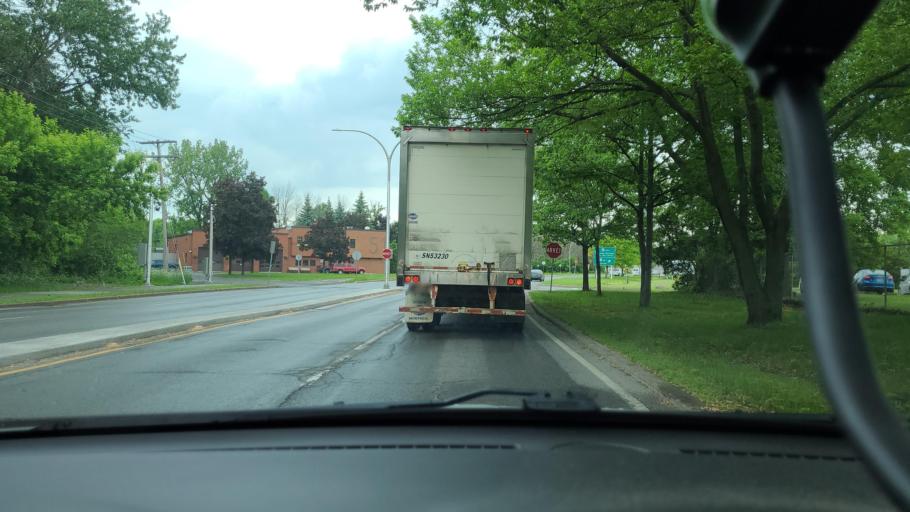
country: CA
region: Quebec
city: Sainte-Anne-de-Bellevue
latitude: 45.4167
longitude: -73.9497
